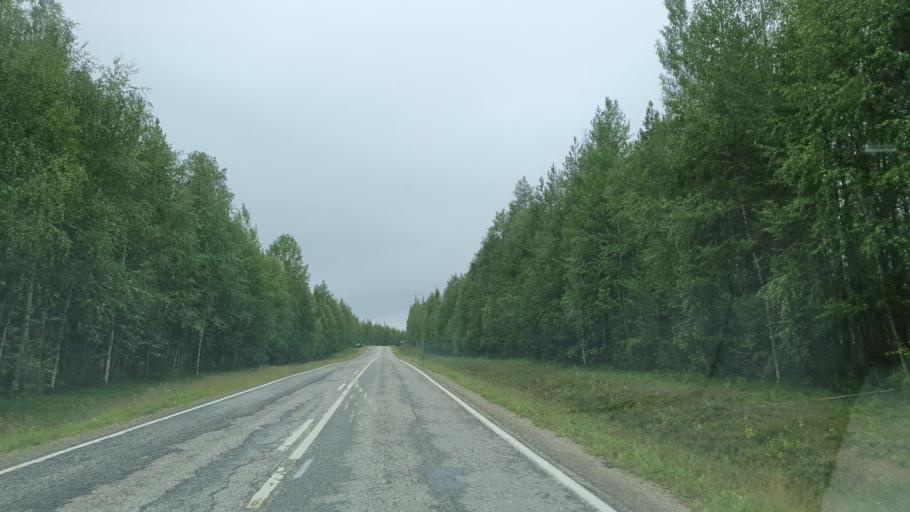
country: FI
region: Lapland
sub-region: Itae-Lappi
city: Pyhaejaervi
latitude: 67.3528
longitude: 27.0009
